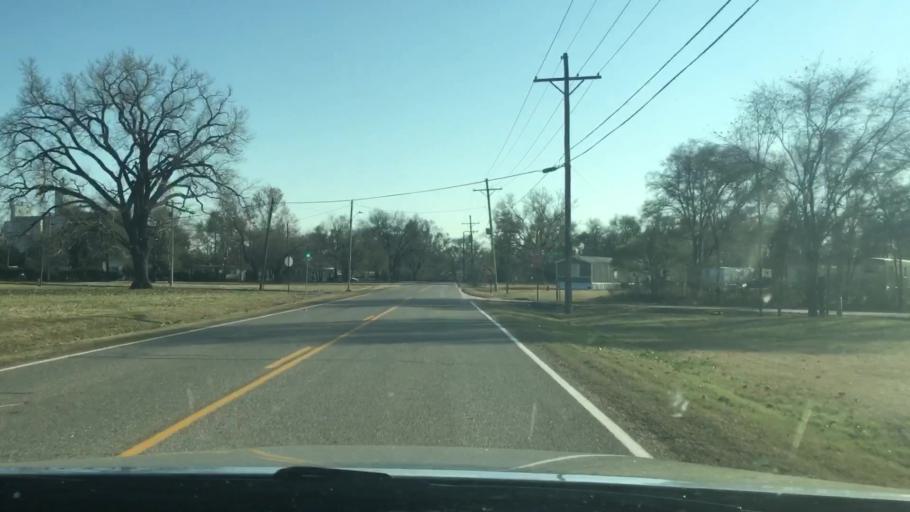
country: US
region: Kansas
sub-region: Reno County
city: Nickerson
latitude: 38.1517
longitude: -98.0873
